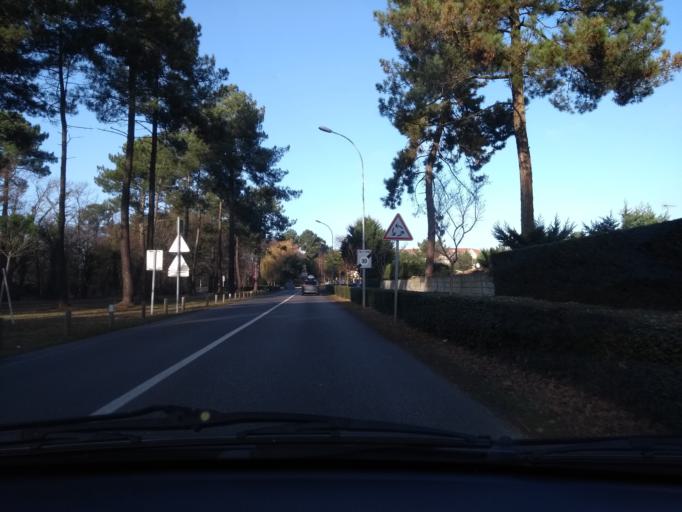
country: FR
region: Aquitaine
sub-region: Departement de la Gironde
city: Gujan-Mestras
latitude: 44.6211
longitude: -1.0731
